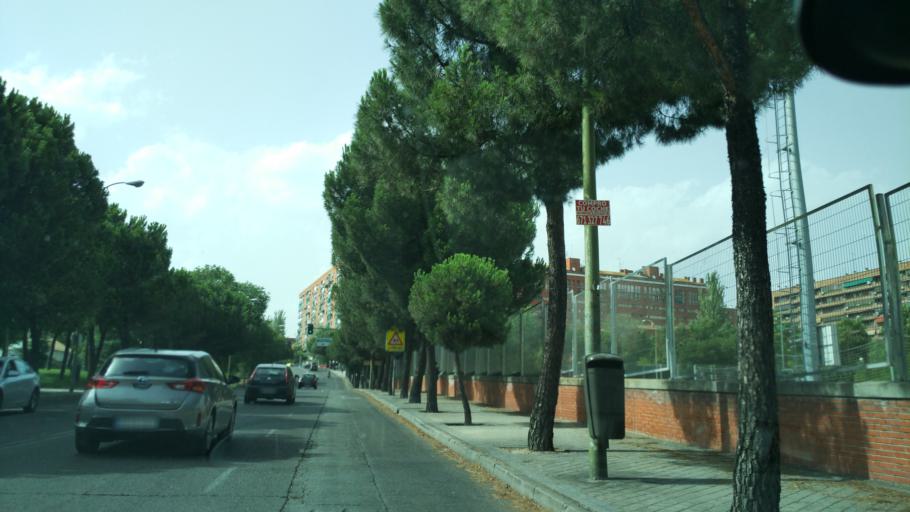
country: ES
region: Madrid
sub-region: Provincia de Madrid
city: Tetuan de las Victorias
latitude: 40.4769
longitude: -3.7217
